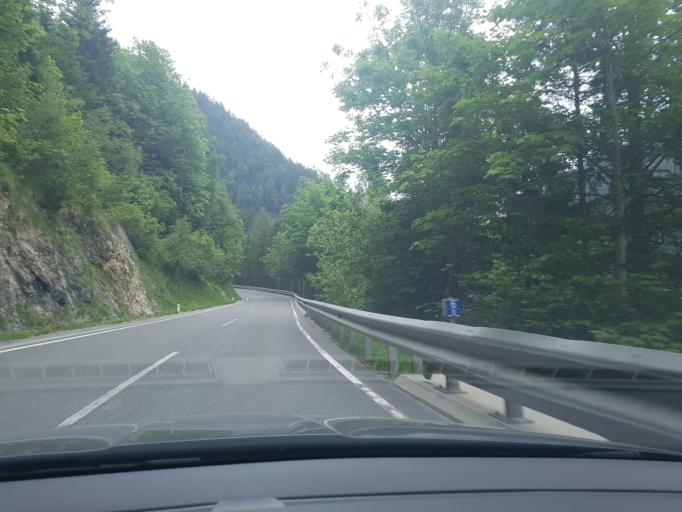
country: AT
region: Salzburg
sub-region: Politischer Bezirk Sankt Johann im Pongau
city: Sankt Johann im Pongau
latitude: 47.3076
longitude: 13.2005
